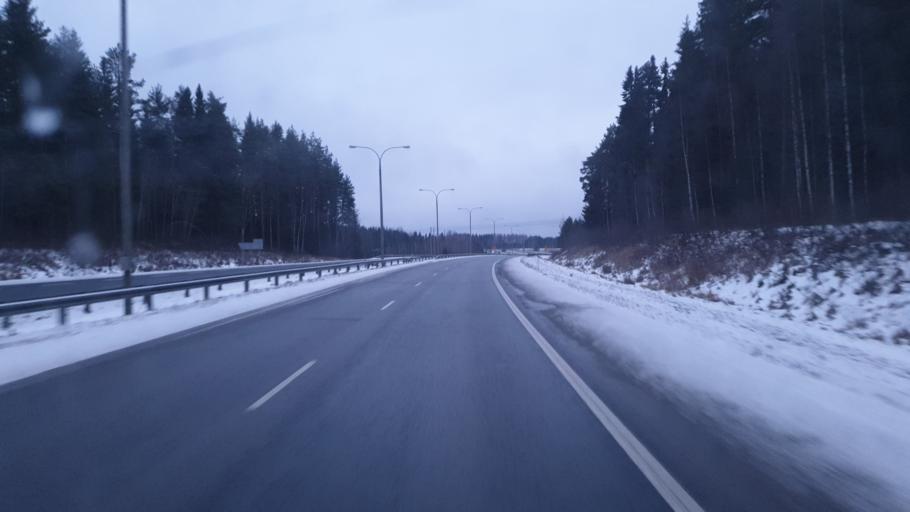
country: FI
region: Northern Savo
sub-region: Kuopio
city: Siilinjaervi
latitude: 63.0536
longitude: 27.6699
